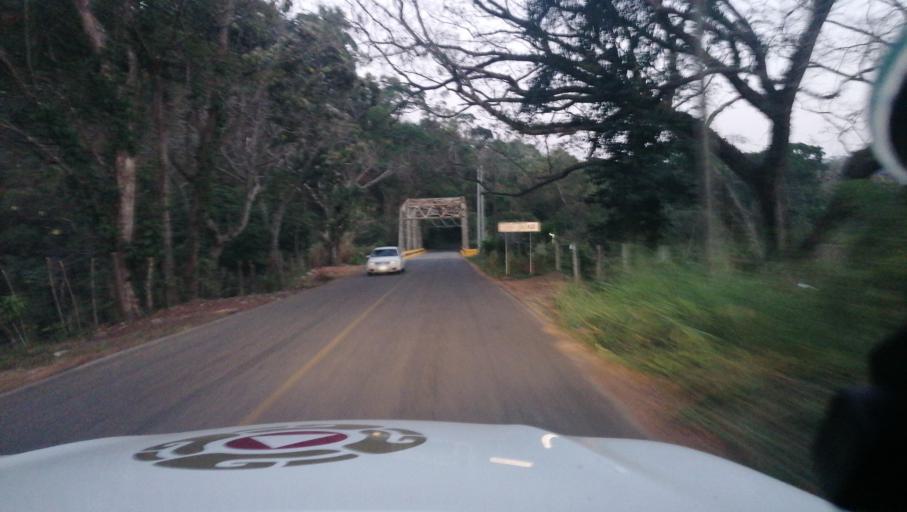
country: MX
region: Chiapas
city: Veinte de Noviembre
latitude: 14.9912
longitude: -92.2435
